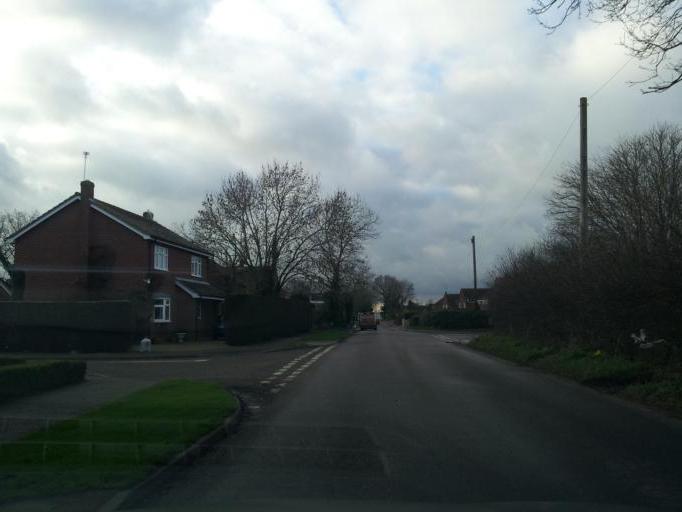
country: GB
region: England
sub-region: Norfolk
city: Lingwood
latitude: 52.6182
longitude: 1.4906
